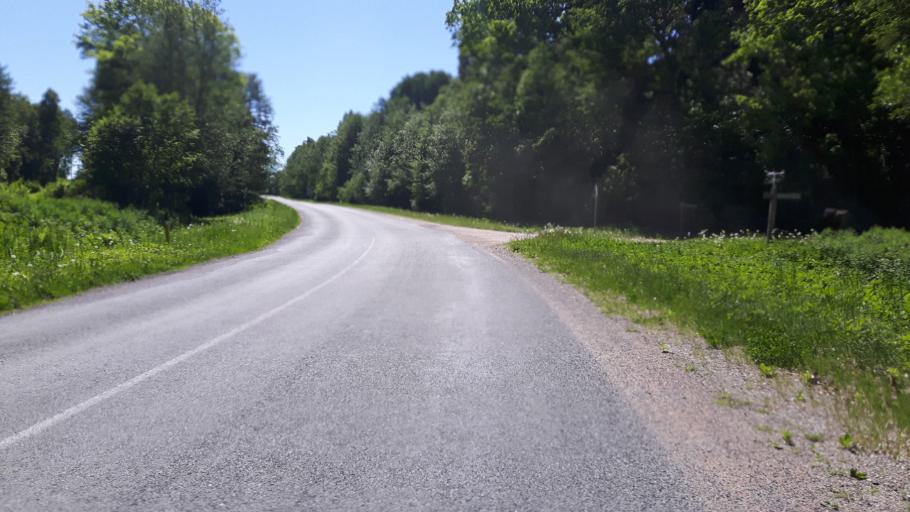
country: EE
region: Harju
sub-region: Kuusalu vald
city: Kuusalu
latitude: 59.5142
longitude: 25.5192
